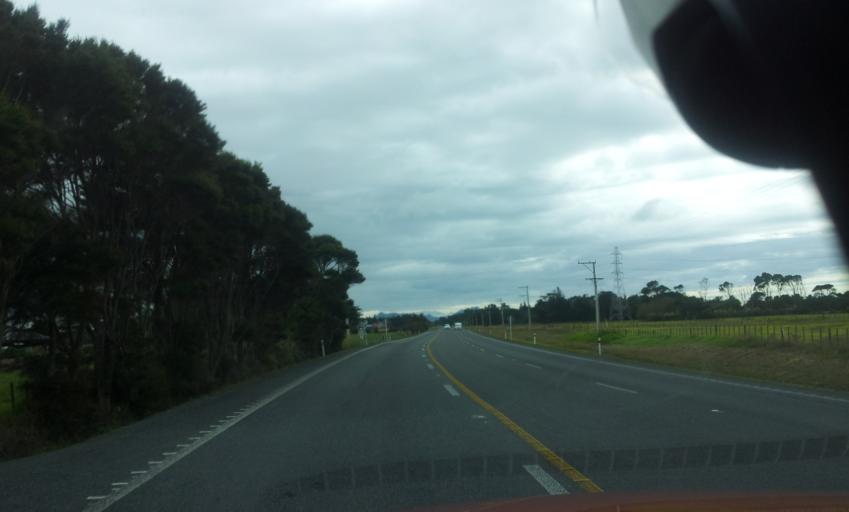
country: NZ
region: Northland
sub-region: Whangarei
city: Ruakaka
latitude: -35.9937
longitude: 174.4210
